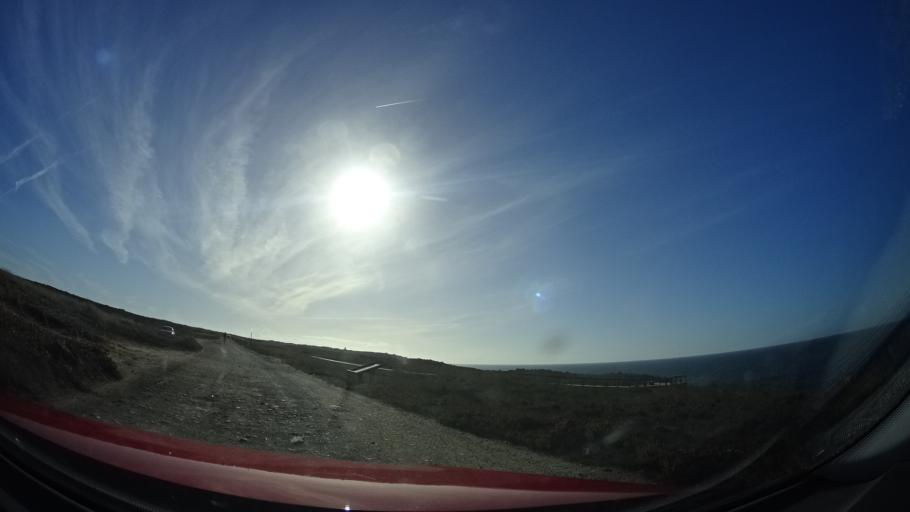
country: PT
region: Faro
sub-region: Vila do Bispo
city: Vila do Bispo
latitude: 37.1972
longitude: -8.9119
